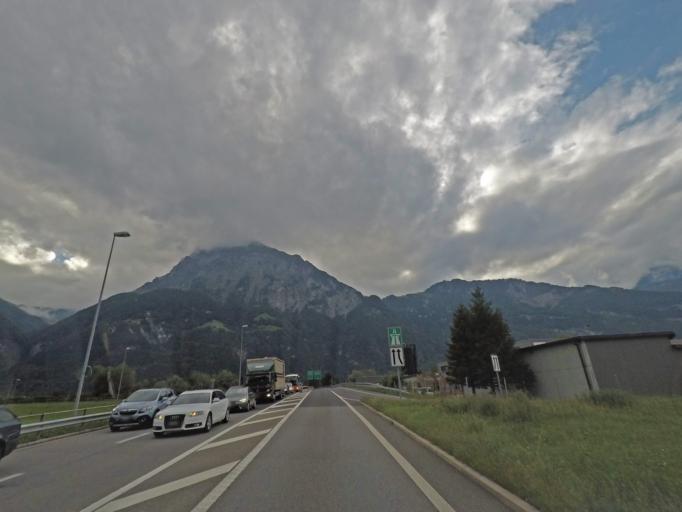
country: CH
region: Uri
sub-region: Uri
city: Flueelen
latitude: 46.8946
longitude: 8.6233
